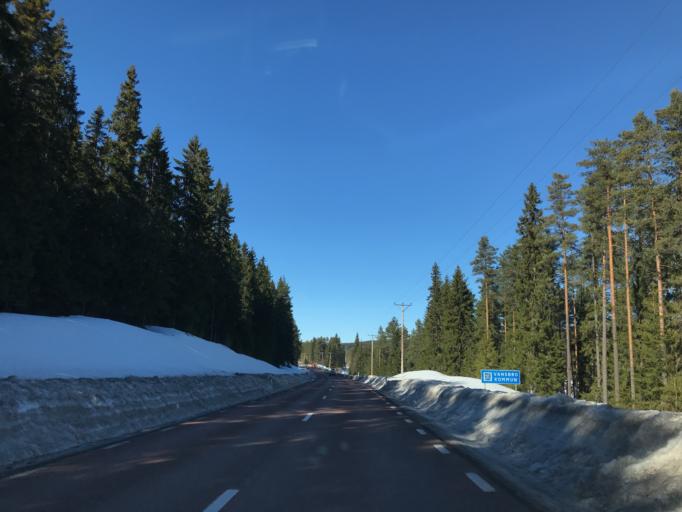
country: SE
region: Vaermland
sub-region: Filipstads Kommun
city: Lesjofors
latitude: 60.2446
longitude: 14.1802
